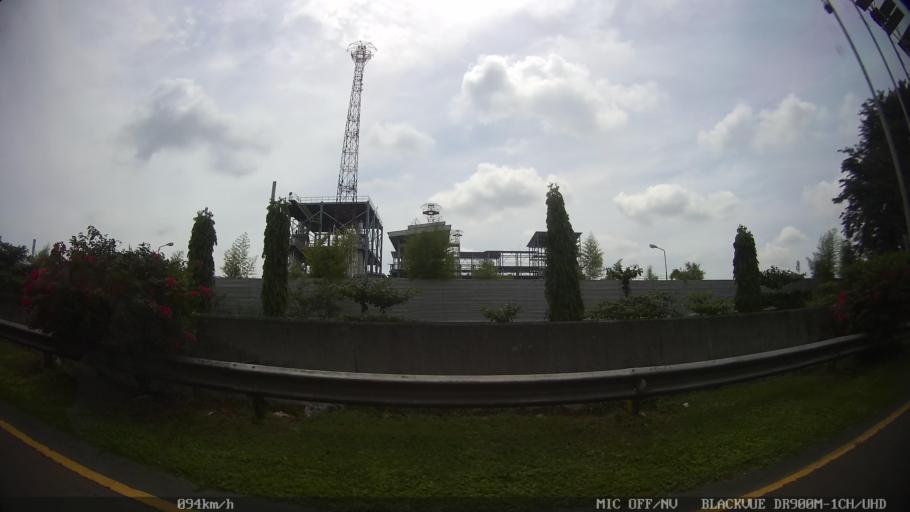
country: ID
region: North Sumatra
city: Labuhan Deli
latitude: 3.6809
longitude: 98.6806
